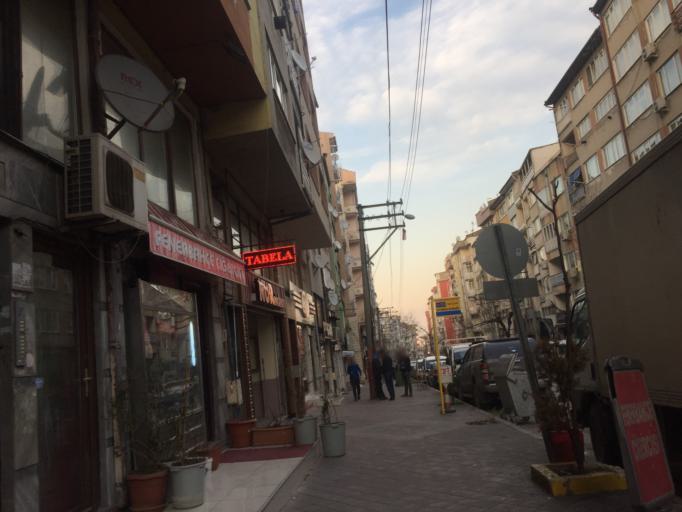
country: TR
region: Bursa
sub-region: Osmangazi
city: Bursa
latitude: 40.1878
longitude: 29.0788
